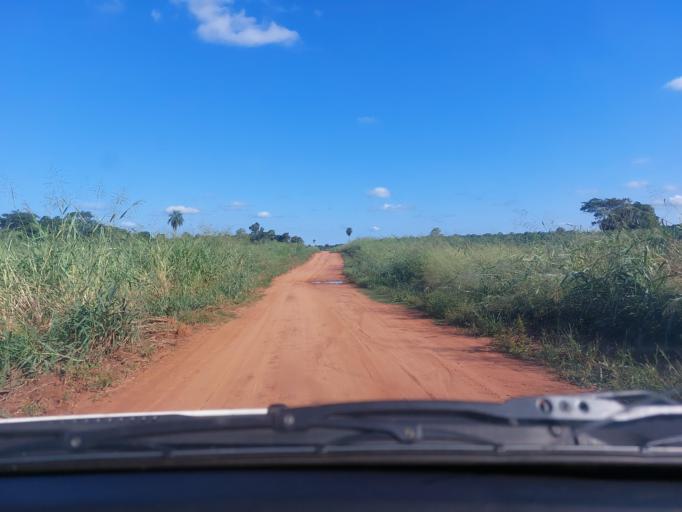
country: PY
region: San Pedro
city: Guayaybi
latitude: -24.5180
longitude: -56.5463
